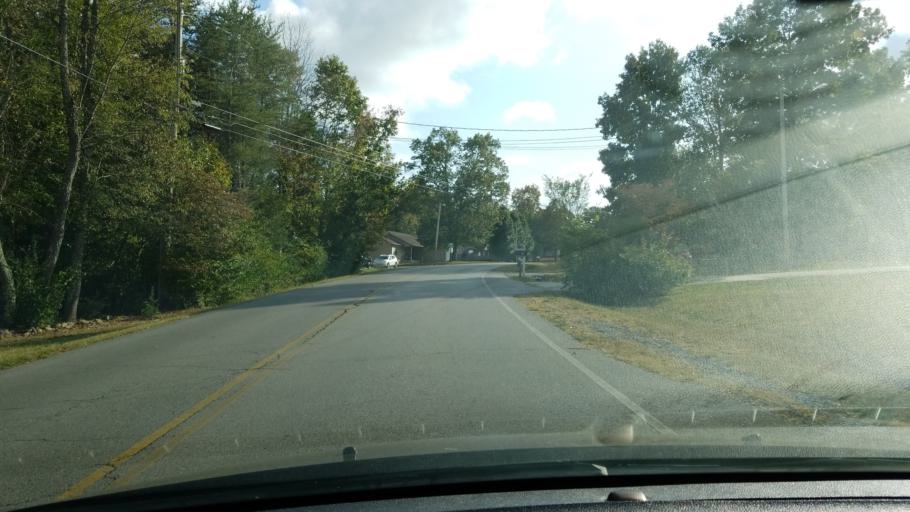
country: US
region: Tennessee
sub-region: Cumberland County
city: Crossville
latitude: 35.9526
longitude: -85.0550
